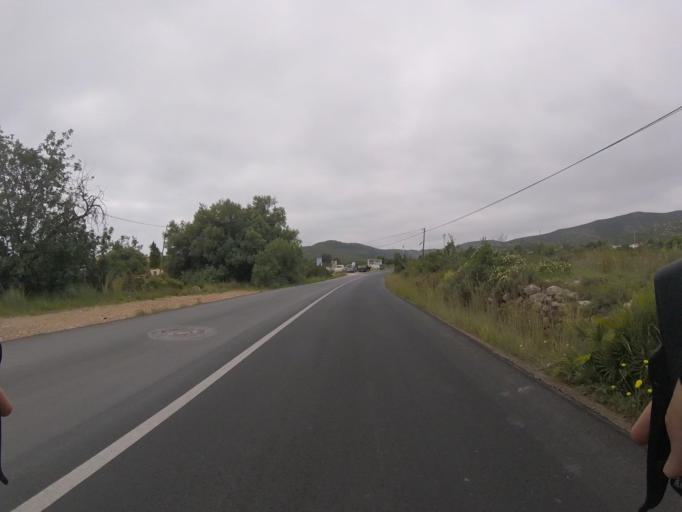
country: ES
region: Valencia
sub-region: Provincia de Castello
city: Peniscola
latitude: 40.3362
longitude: 0.3743
